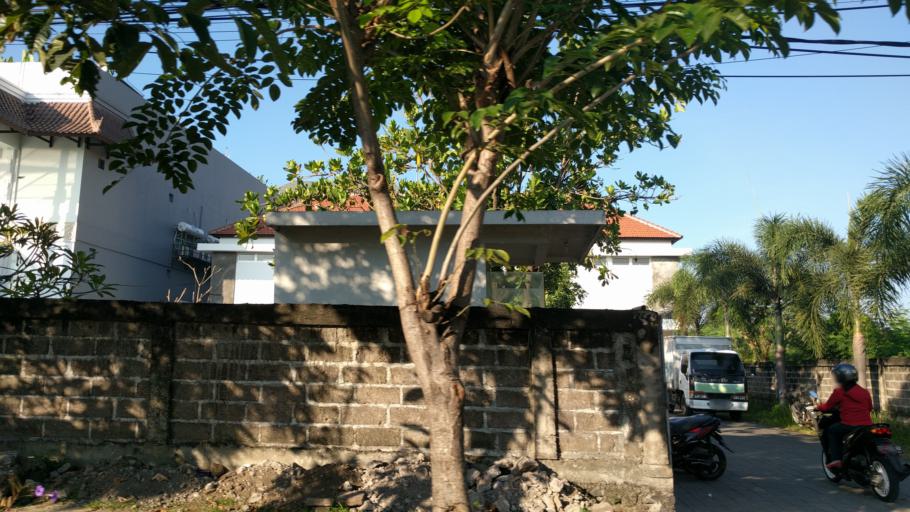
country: ID
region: Bali
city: Kuta
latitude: -8.7012
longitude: 115.1791
